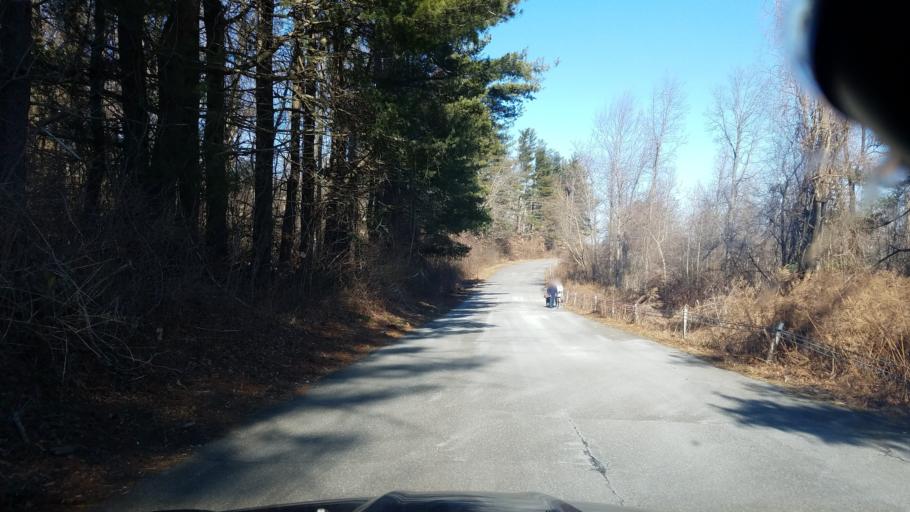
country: US
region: Connecticut
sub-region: New Haven County
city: Heritage Village
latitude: 41.4943
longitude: -73.2732
